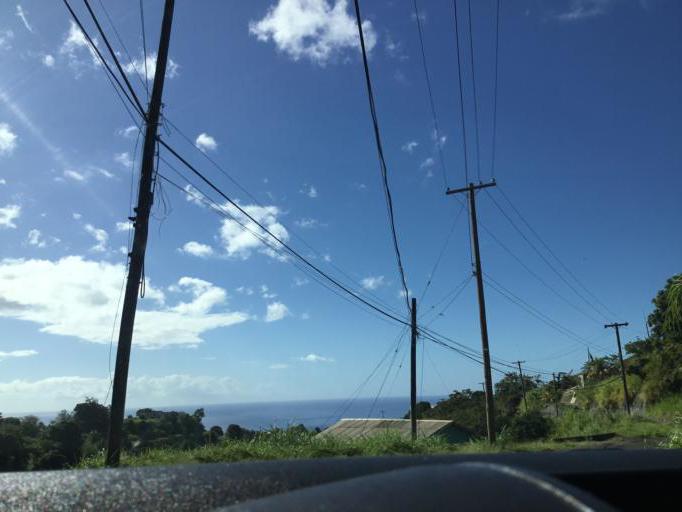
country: VC
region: Saint David
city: Chateaubelair
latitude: 13.2746
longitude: -61.2462
